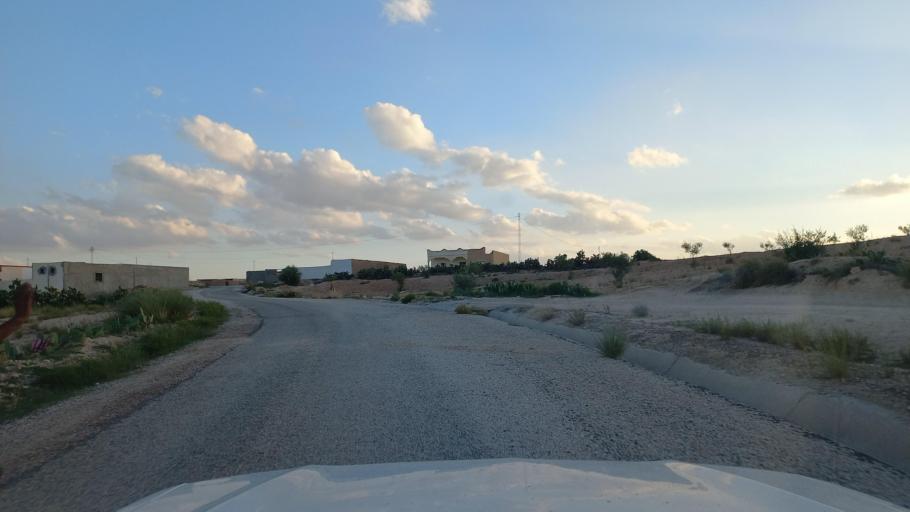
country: TN
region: Al Qasrayn
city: Sbiba
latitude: 35.3740
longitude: 9.0619
